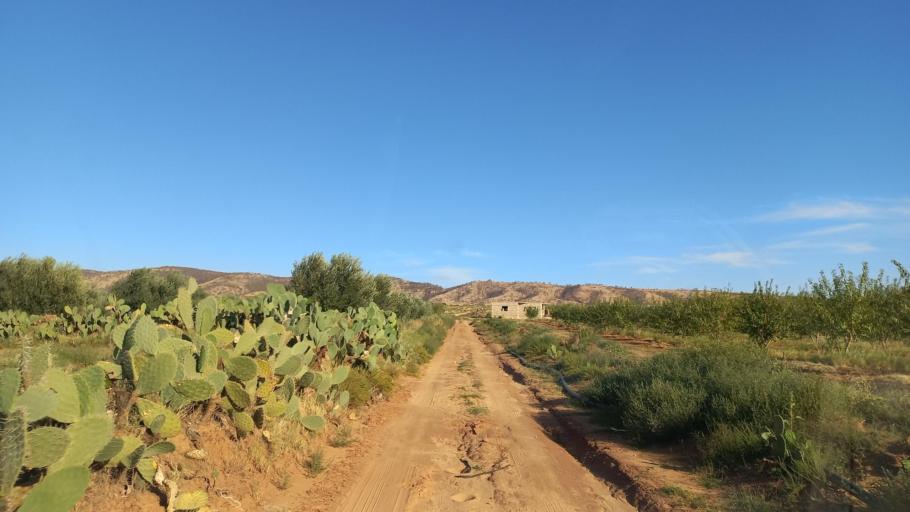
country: TN
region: Al Qasrayn
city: Sbiba
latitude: 35.3350
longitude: 9.1273
